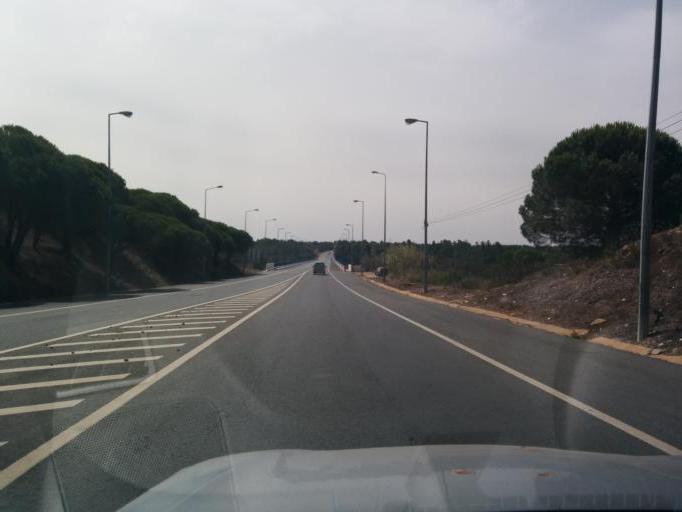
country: PT
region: Beja
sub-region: Odemira
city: Vila Nova de Milfontes
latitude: 37.7293
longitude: -8.7714
